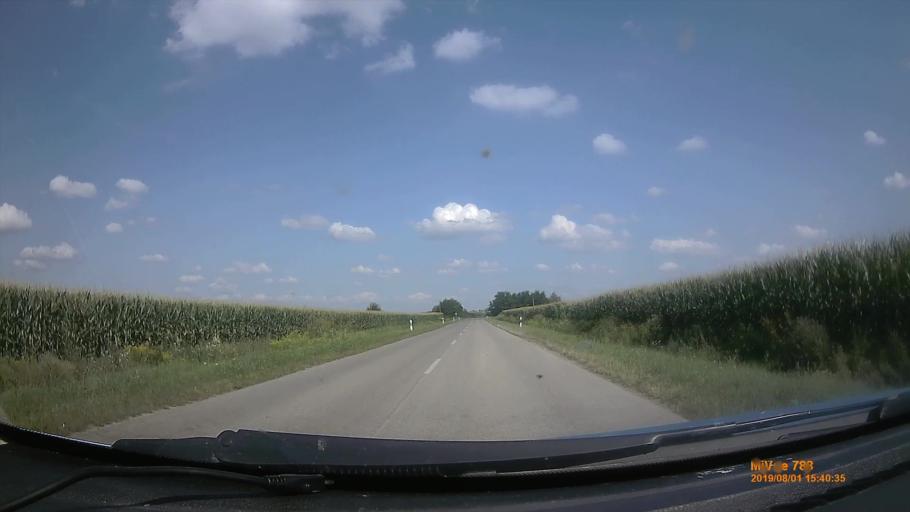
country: HU
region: Baranya
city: Szentlorinc
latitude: 45.9874
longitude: 17.9550
